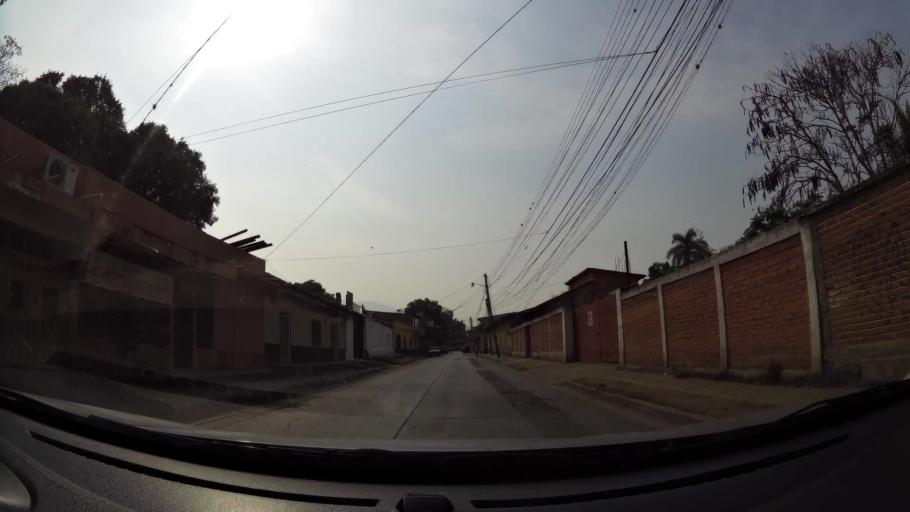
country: HN
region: Comayagua
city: Comayagua
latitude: 14.4637
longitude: -87.6453
